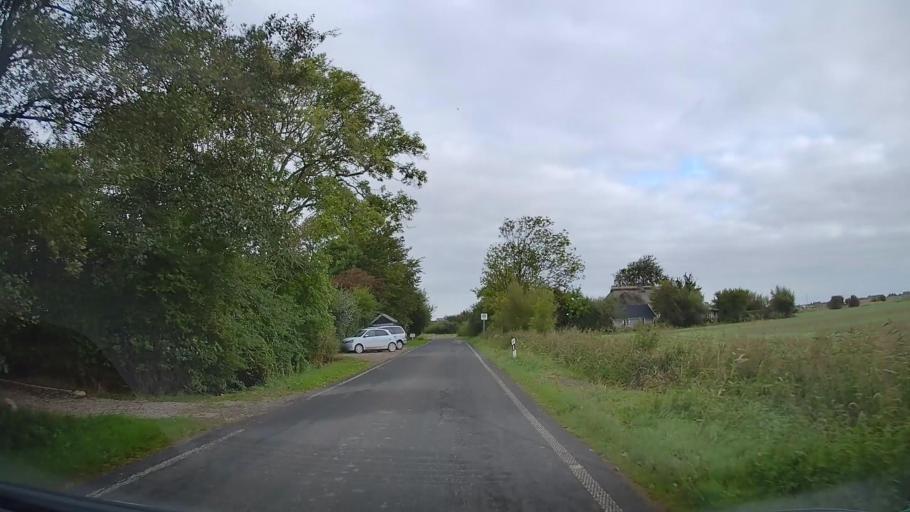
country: DE
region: Schleswig-Holstein
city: Emmelsbull-Horsbull
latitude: 54.8335
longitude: 8.6611
